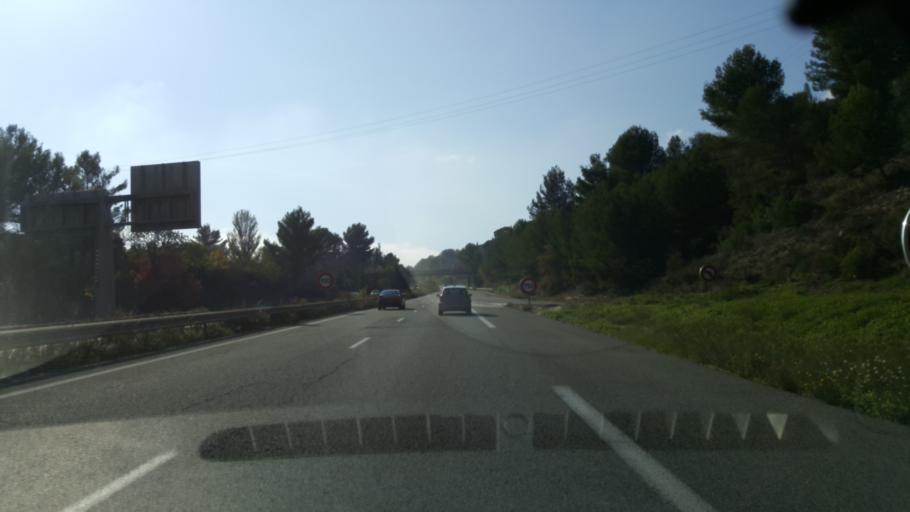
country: FR
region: Provence-Alpes-Cote d'Azur
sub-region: Departement des Bouches-du-Rhone
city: Aubagne
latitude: 43.3039
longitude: 5.5708
